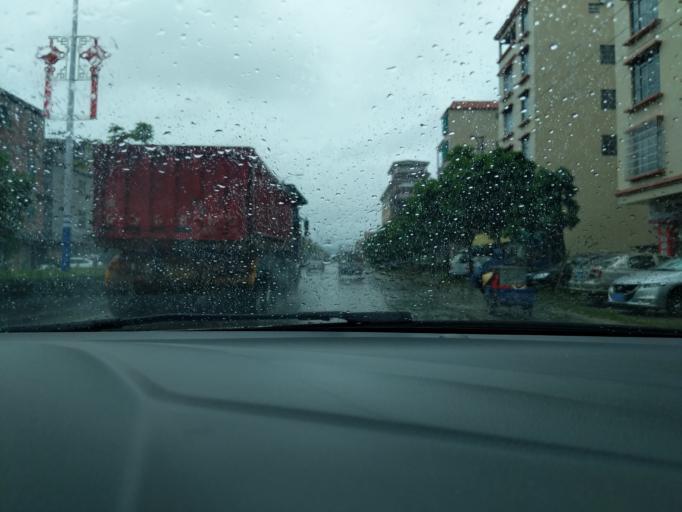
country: CN
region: Guangdong
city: Pingshi
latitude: 22.2053
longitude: 112.3260
